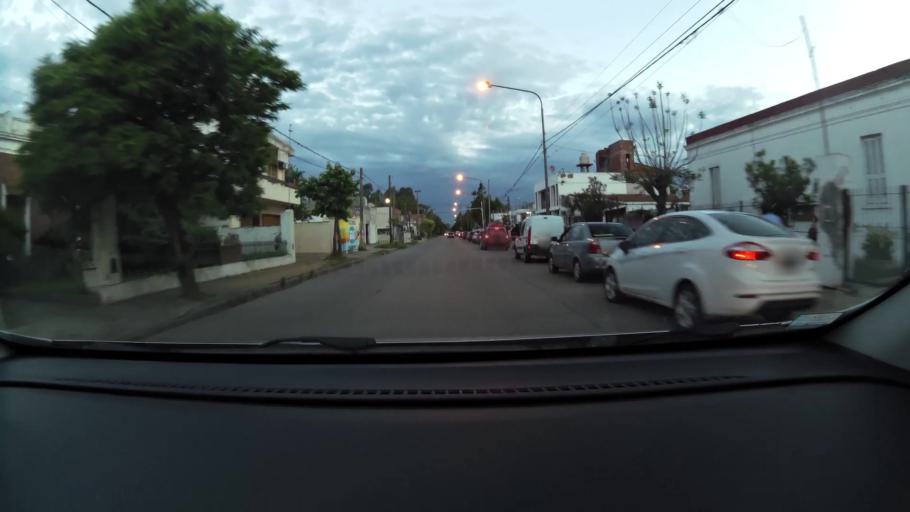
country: AR
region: Buenos Aires
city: San Nicolas de los Arroyos
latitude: -33.3446
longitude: -60.1940
